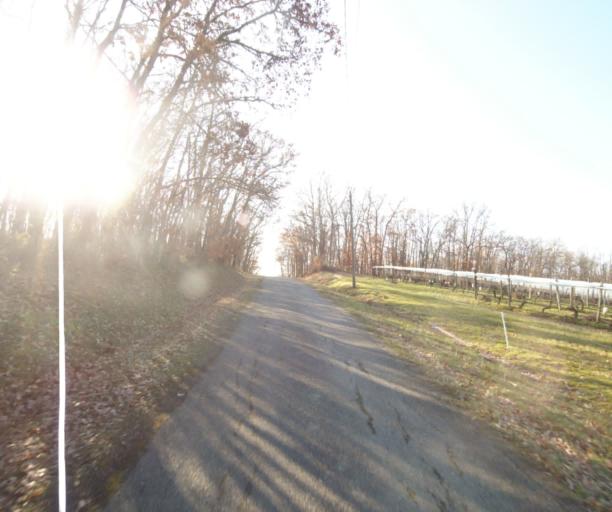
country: FR
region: Midi-Pyrenees
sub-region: Departement du Tarn-et-Garonne
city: Moissac
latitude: 44.1287
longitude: 1.0494
